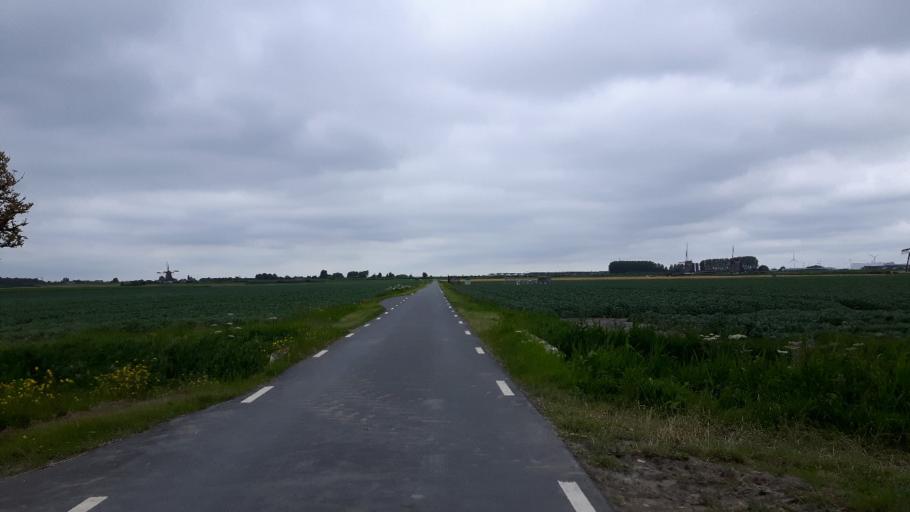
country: NL
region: South Holland
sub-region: Gemeente Lansingerland
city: Bleiswijk
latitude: 52.0252
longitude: 4.5722
